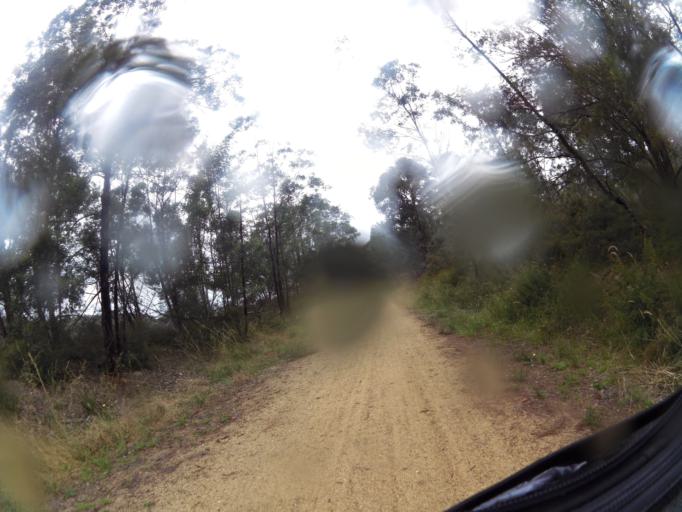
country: AU
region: Victoria
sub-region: East Gippsland
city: Bairnsdale
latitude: -37.7473
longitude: 147.8108
